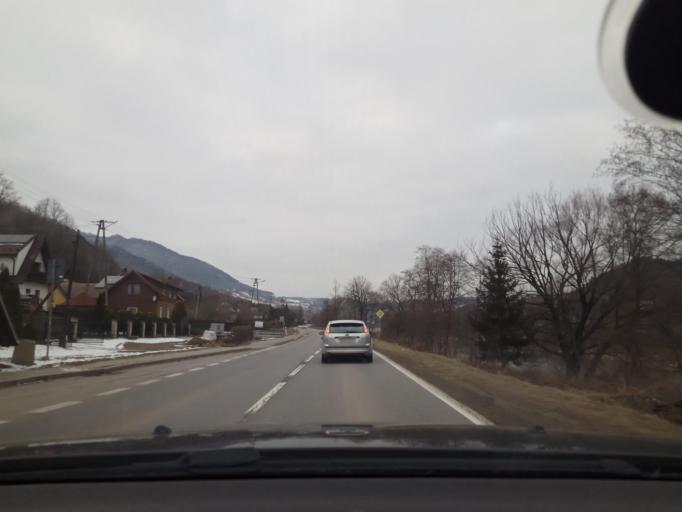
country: PL
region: Lesser Poland Voivodeship
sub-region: Powiat nowotarski
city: Kroscienko nad Dunajcem
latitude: 49.4855
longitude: 20.4107
